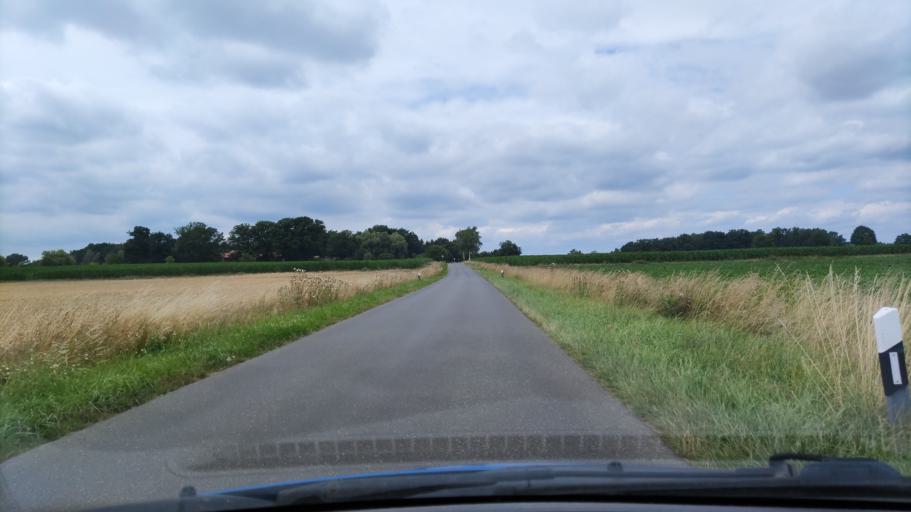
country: DE
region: Lower Saxony
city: Weste
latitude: 53.0664
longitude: 10.6960
